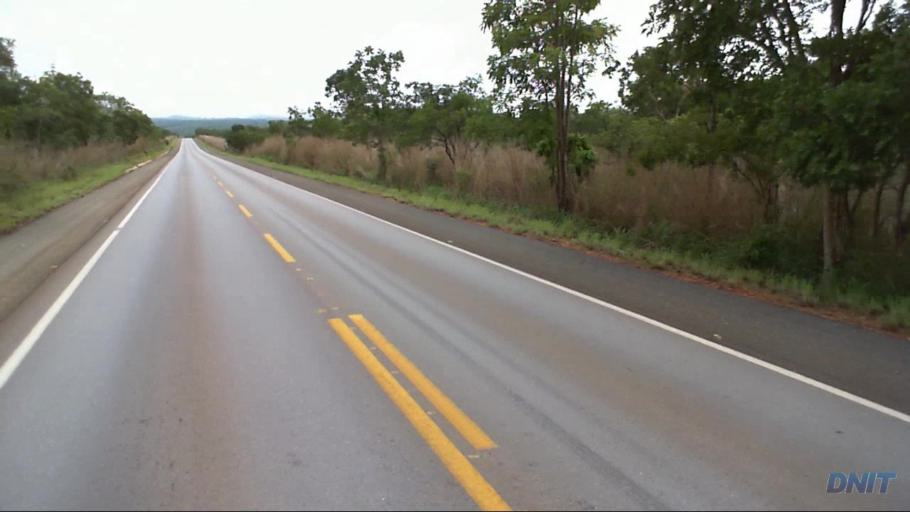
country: BR
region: Goias
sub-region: Uruacu
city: Uruacu
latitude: -14.7629
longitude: -49.0625
